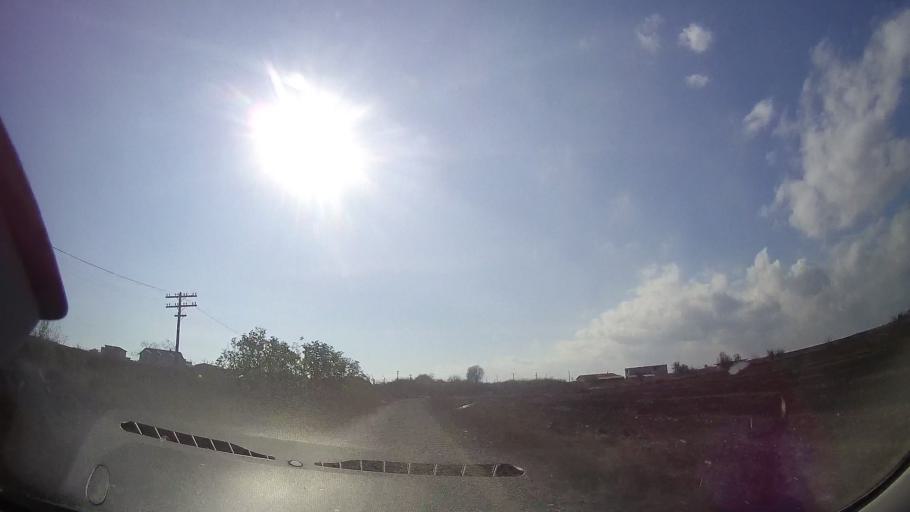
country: RO
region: Constanta
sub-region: Comuna Costinesti
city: Costinesti
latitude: 43.9644
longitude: 28.6391
